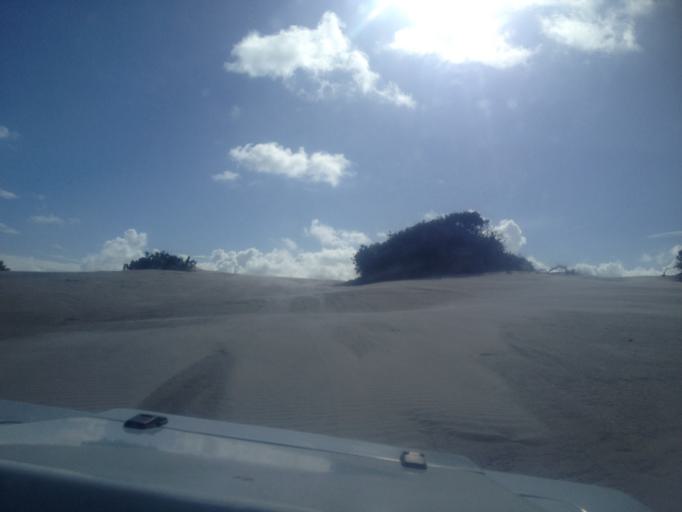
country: BR
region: Sergipe
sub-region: Indiaroba
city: Indiaroba
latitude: -11.4751
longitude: -37.3758
